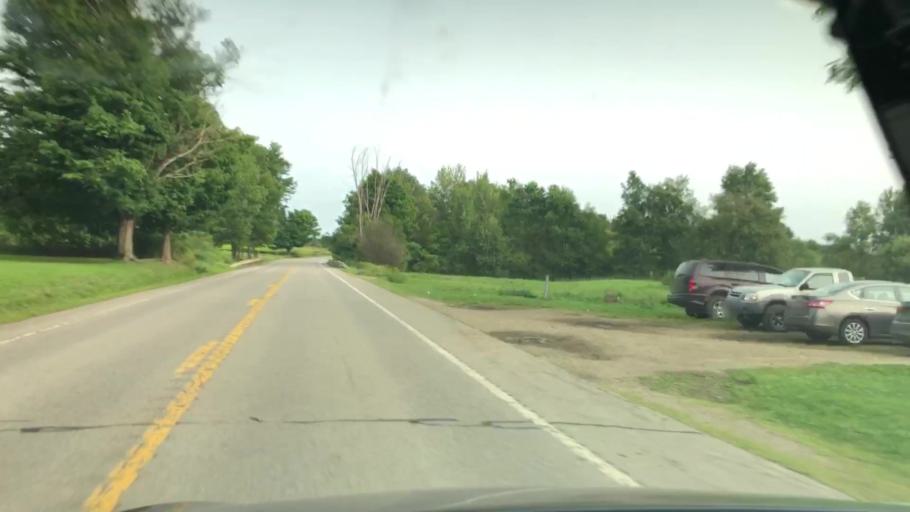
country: US
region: Pennsylvania
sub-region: Erie County
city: Union City
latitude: 41.8160
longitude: -79.8049
